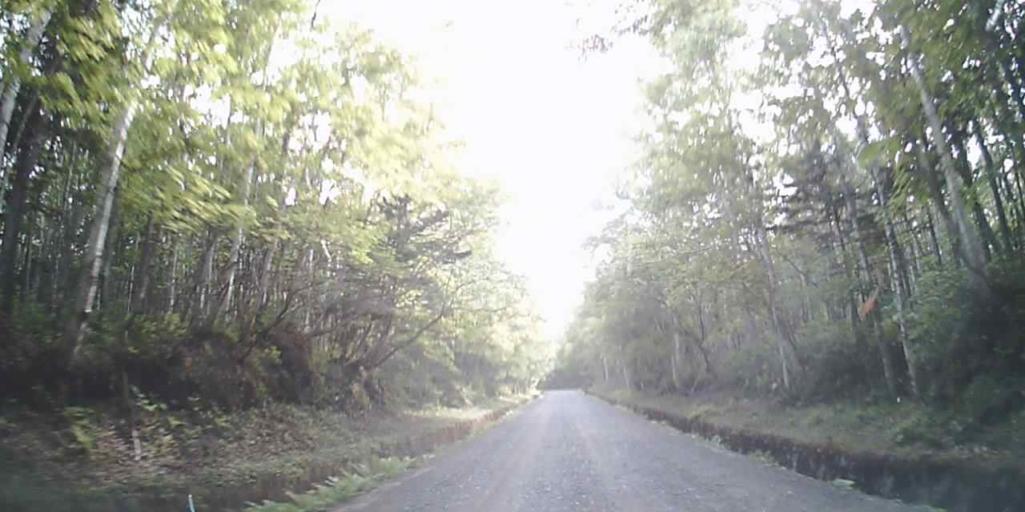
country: JP
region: Hokkaido
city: Shiraoi
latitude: 42.7140
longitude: 141.4026
